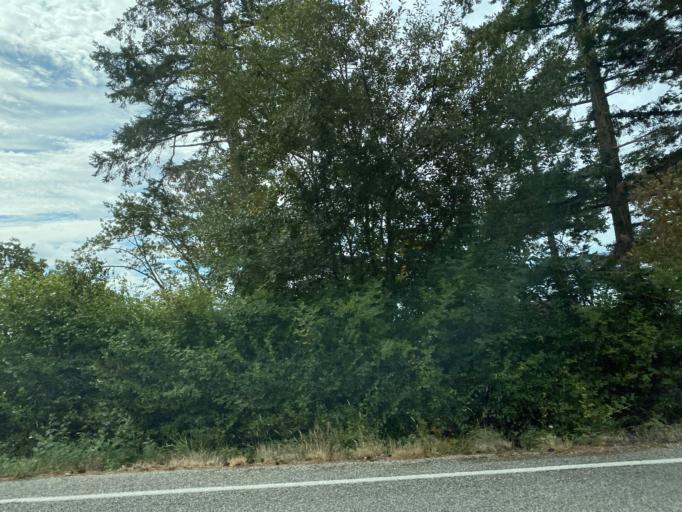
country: US
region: Washington
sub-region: Island County
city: Coupeville
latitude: 48.2393
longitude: -122.6958
